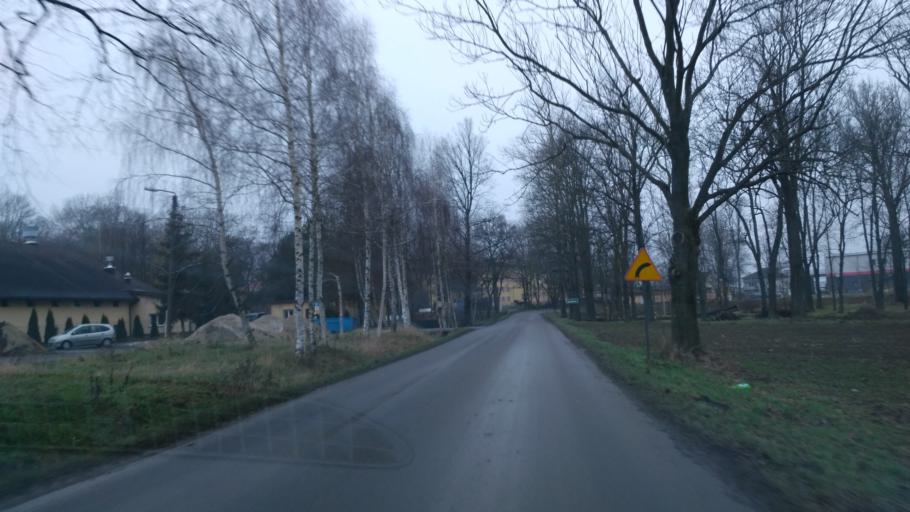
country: PL
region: Subcarpathian Voivodeship
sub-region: Powiat przeworski
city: Zarzecze
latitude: 49.9847
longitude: 22.5461
